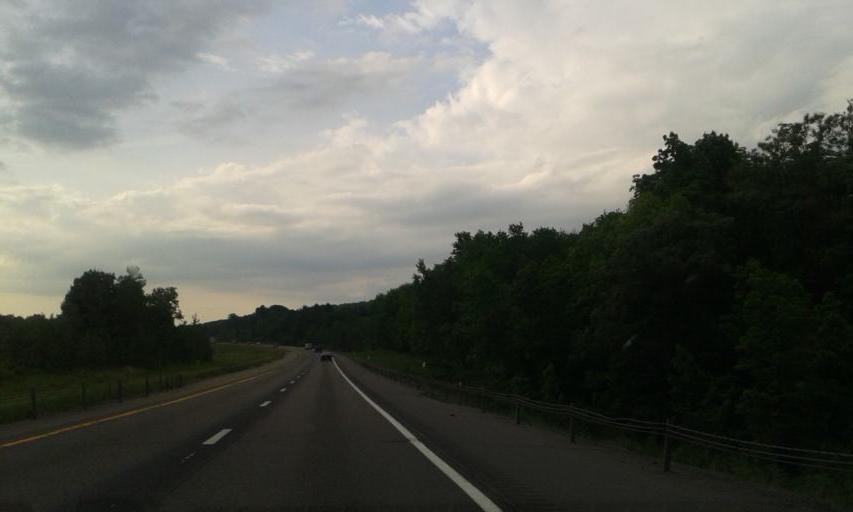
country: US
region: New York
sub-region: Broome County
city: Chenango Bridge
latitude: 42.0713
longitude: -75.7999
